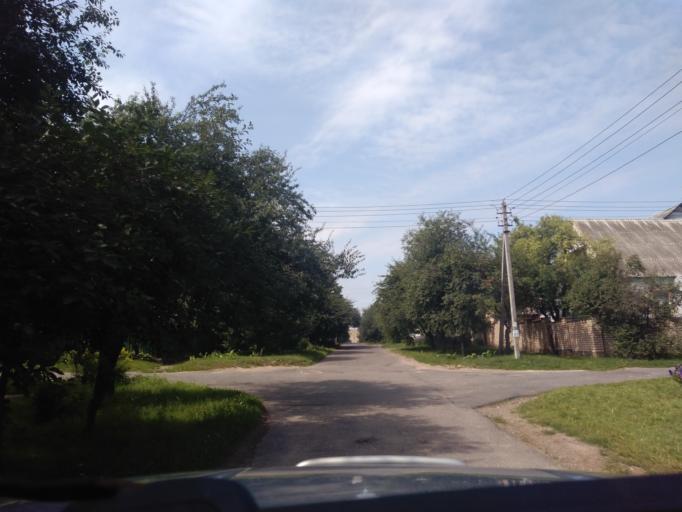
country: BY
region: Minsk
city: Novoye Medvezhino
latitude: 53.8791
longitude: 27.4952
